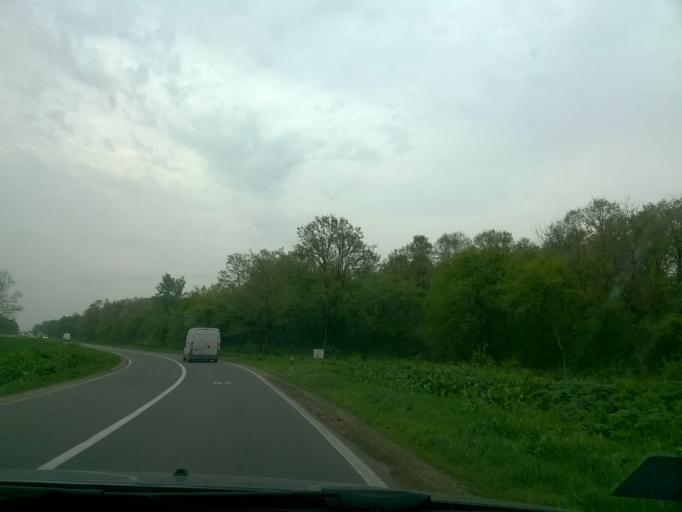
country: RS
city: Platicevo
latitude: 44.8435
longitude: 19.7670
